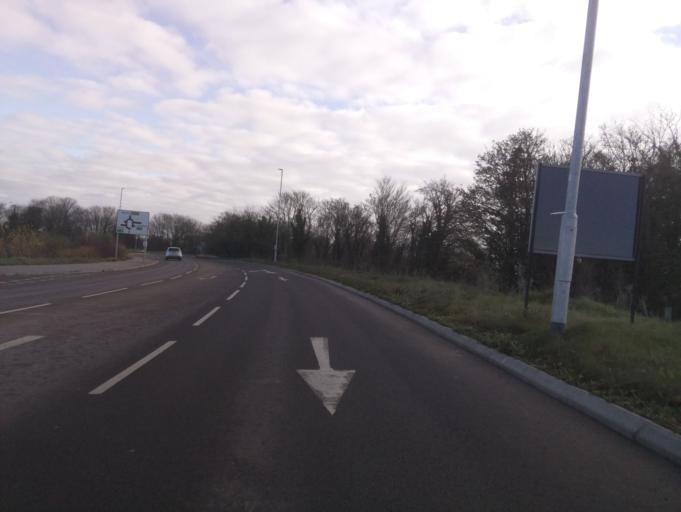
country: GB
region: England
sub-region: Staffordshire
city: Burton upon Trent
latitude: 52.7892
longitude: -1.6785
